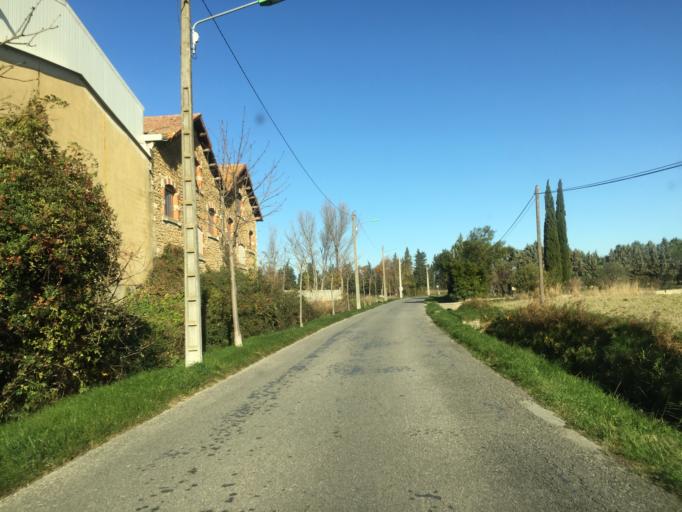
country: FR
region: Provence-Alpes-Cote d'Azur
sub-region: Departement du Vaucluse
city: Bedarrides
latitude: 44.0464
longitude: 4.9004
